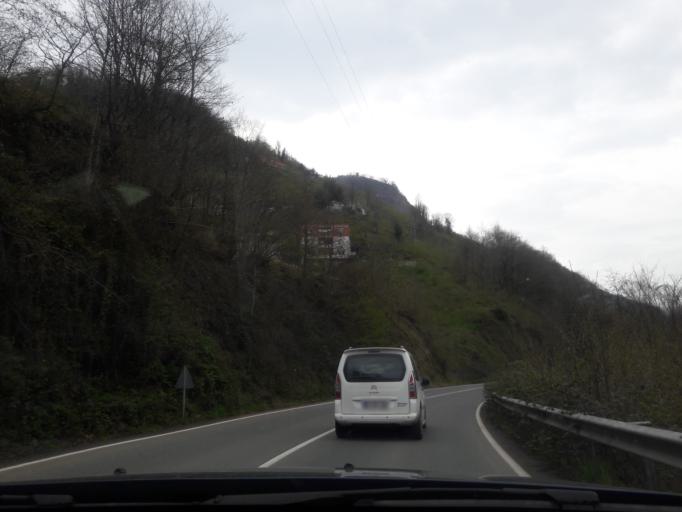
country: TR
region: Trabzon
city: Salpazari
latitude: 40.9819
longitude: 39.1972
